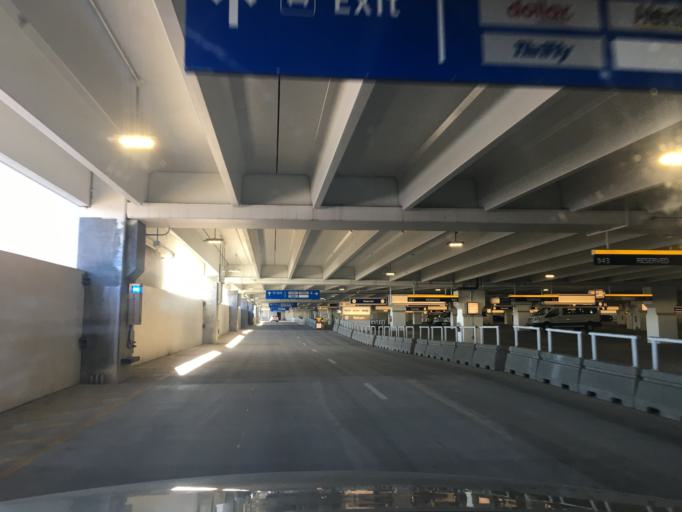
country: US
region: Illinois
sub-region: Cook County
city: Rosemont
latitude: 41.9938
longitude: -87.8804
